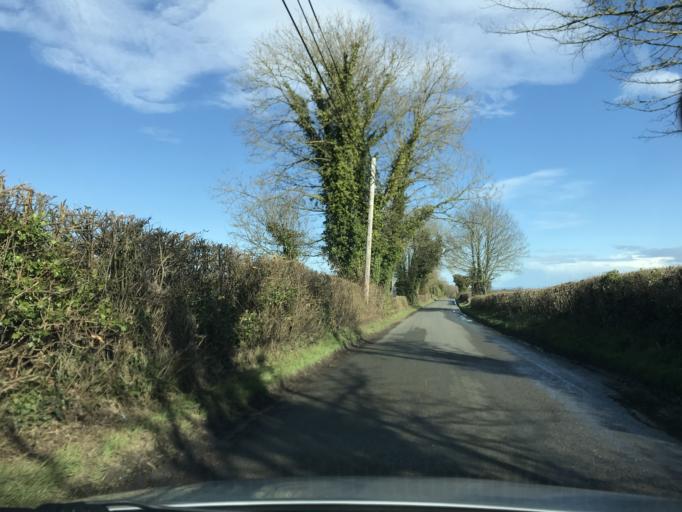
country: GB
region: England
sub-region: Somerset
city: Creech Saint Michael
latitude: 50.9602
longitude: -3.0472
